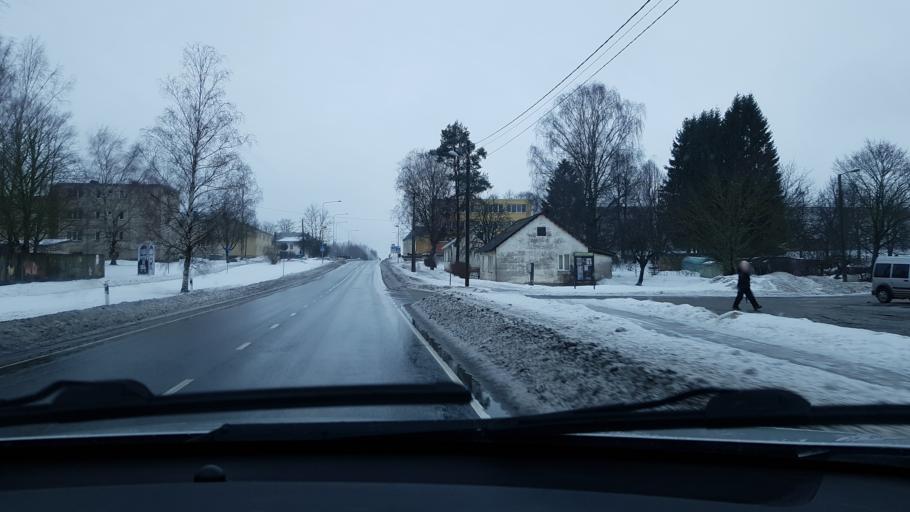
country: EE
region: Jaervamaa
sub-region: Tueri vald
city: Tueri
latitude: 58.8121
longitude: 25.4079
